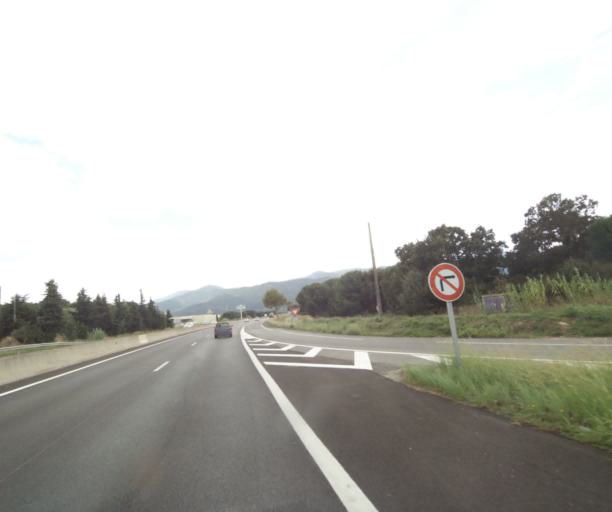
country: FR
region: Languedoc-Roussillon
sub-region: Departement des Pyrenees-Orientales
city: Argelers
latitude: 42.5623
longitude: 3.0059
